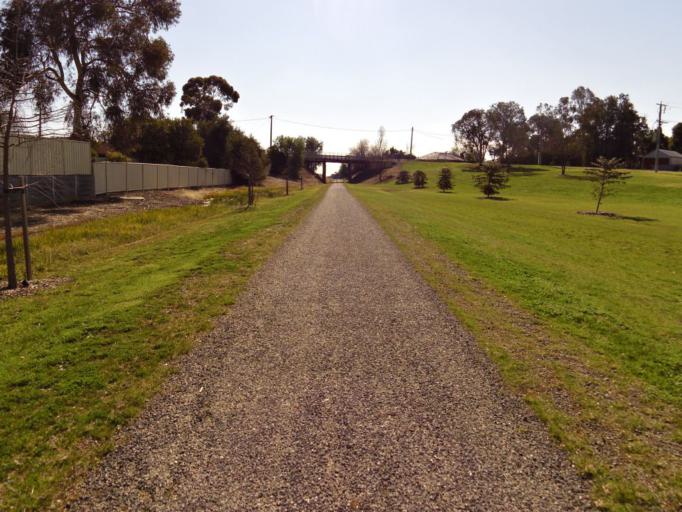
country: AU
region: New South Wales
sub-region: Corowa Shire
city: Corowa
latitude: -36.0535
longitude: 146.4623
